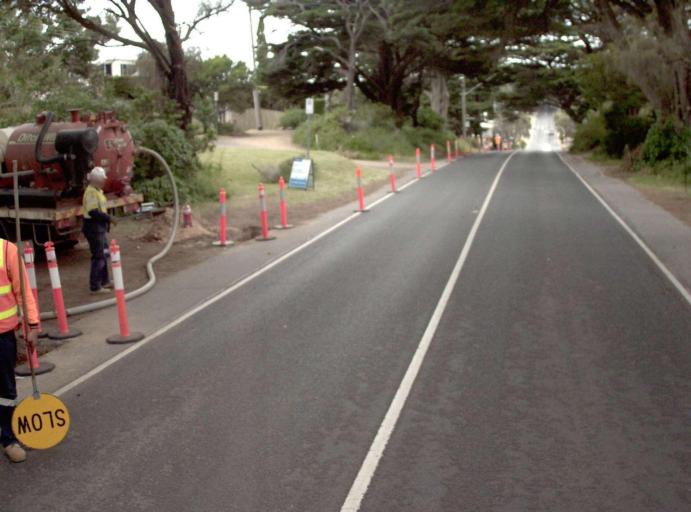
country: AU
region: Victoria
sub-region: Mornington Peninsula
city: Sorrento
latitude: -38.3197
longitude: 144.7110
